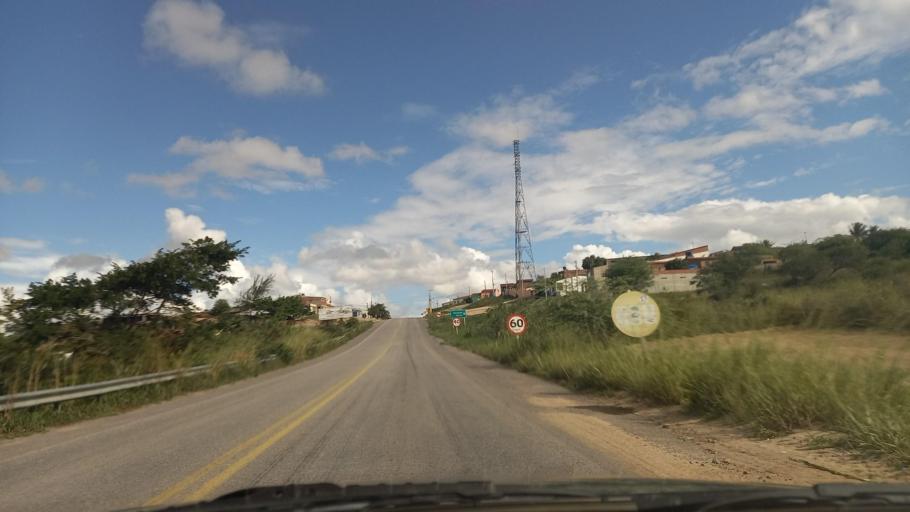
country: BR
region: Pernambuco
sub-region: Sao Joao
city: Sao Joao
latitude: -8.7510
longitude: -36.4311
